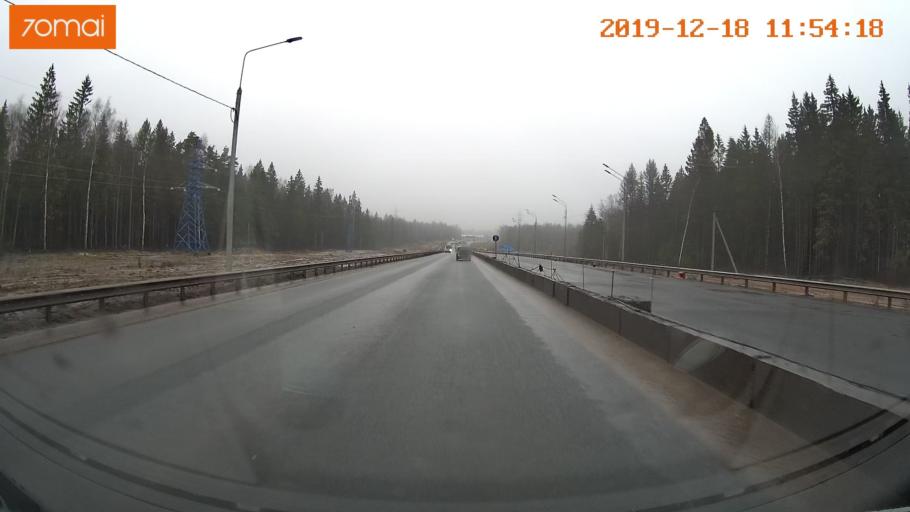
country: RU
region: Moskovskaya
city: Yershovo
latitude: 55.8140
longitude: 36.9184
